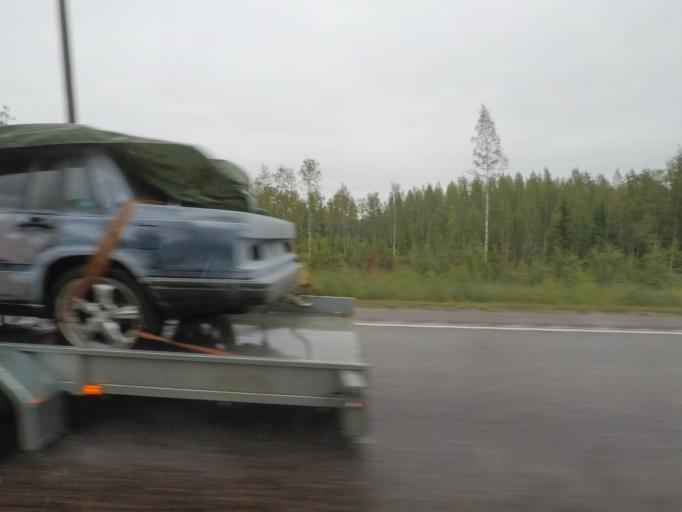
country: FI
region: Northern Savo
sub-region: Varkaus
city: Leppaevirta
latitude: 62.4681
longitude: 27.7780
